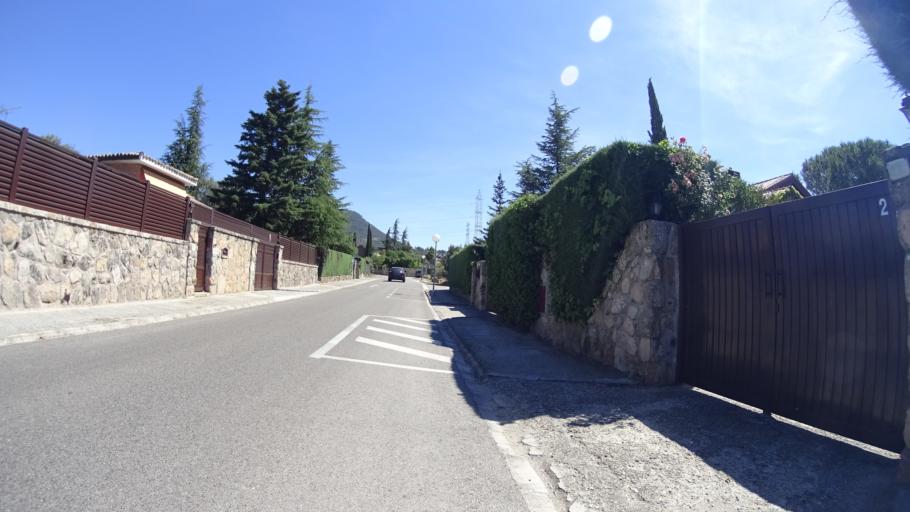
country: ES
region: Madrid
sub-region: Provincia de Madrid
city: Hoyo de Manzanares
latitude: 40.6118
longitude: -3.9356
